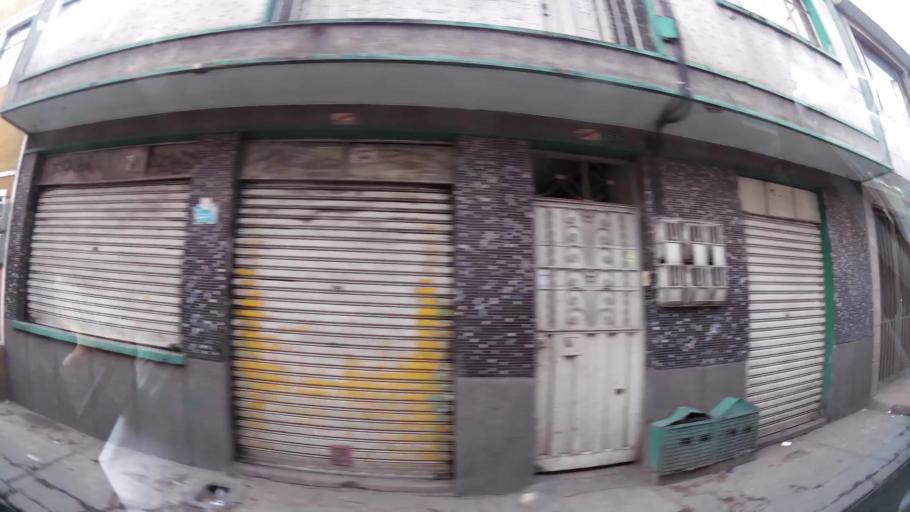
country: CO
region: Bogota D.C.
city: Barrio San Luis
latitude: 4.6861
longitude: -74.0871
